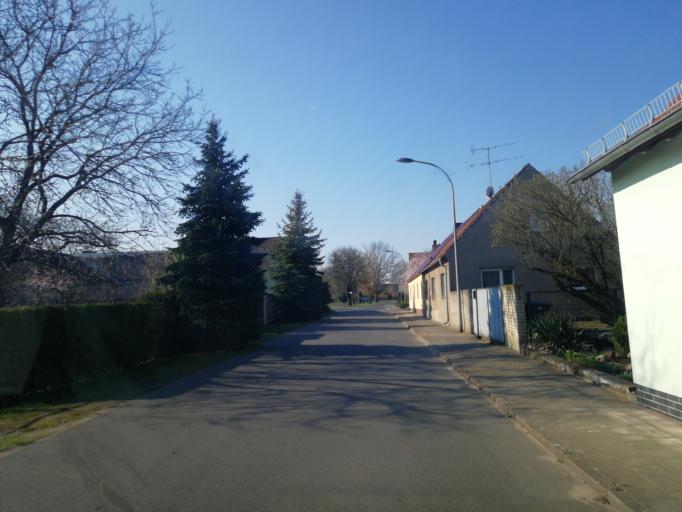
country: DE
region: Brandenburg
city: Drahnsdorf
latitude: 51.8691
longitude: 13.5914
